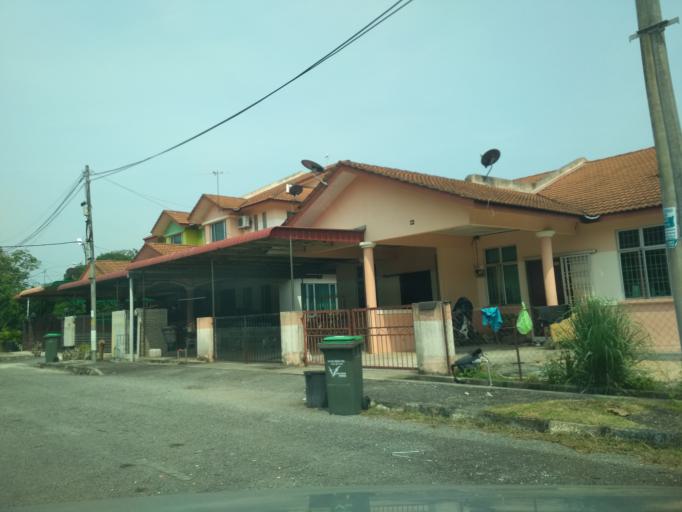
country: MY
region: Kedah
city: Kulim
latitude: 5.3749
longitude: 100.5678
